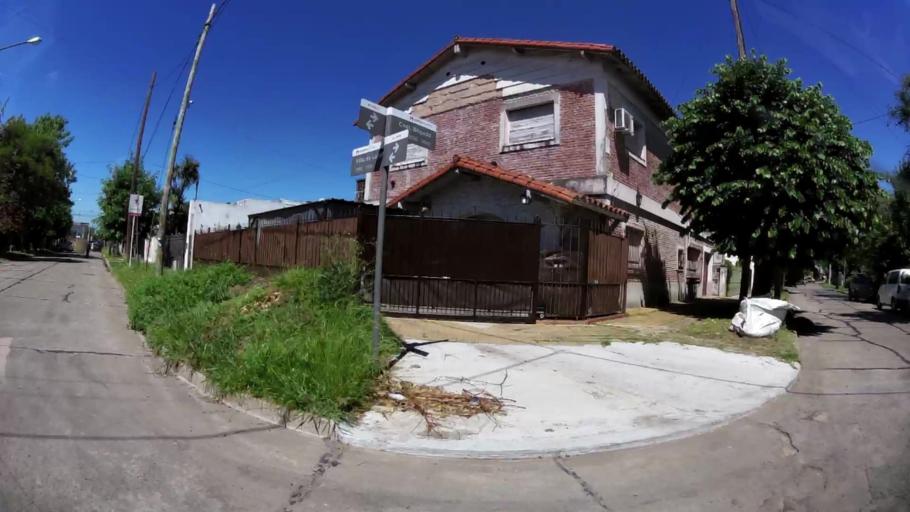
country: AR
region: Buenos Aires
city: Ituzaingo
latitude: -34.6608
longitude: -58.6422
